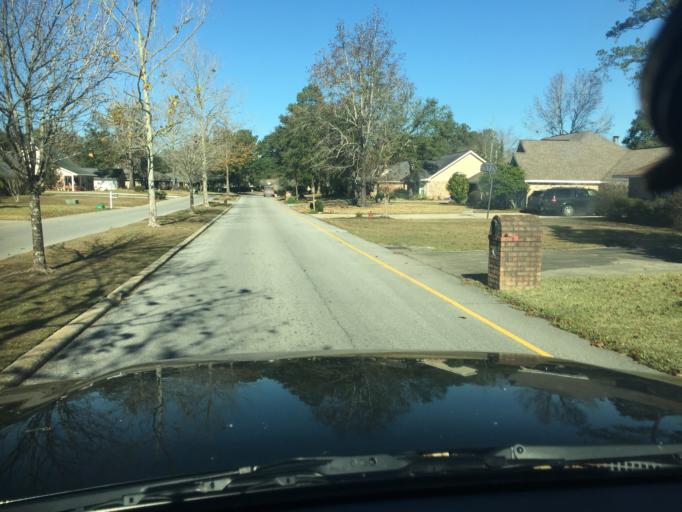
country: US
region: Louisiana
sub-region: Saint Tammany Parish
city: Slidell
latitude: 30.2974
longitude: -89.7234
